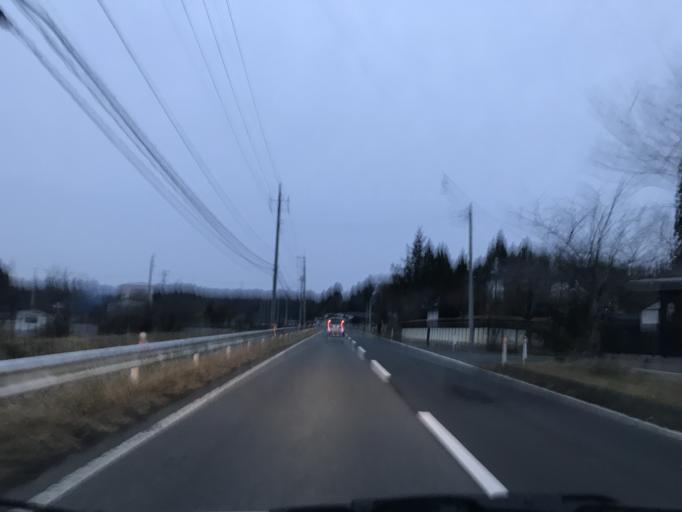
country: JP
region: Iwate
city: Ichinoseki
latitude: 38.8041
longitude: 141.1161
